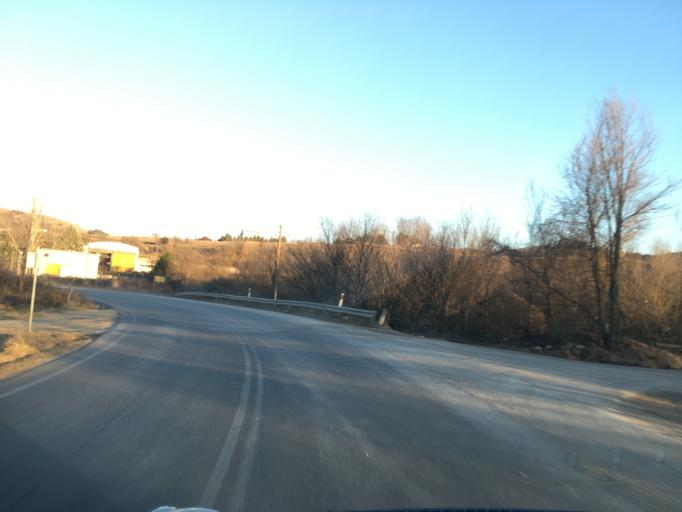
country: GR
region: West Macedonia
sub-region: Nomos Kozanis
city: Koila
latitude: 40.3244
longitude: 21.7826
